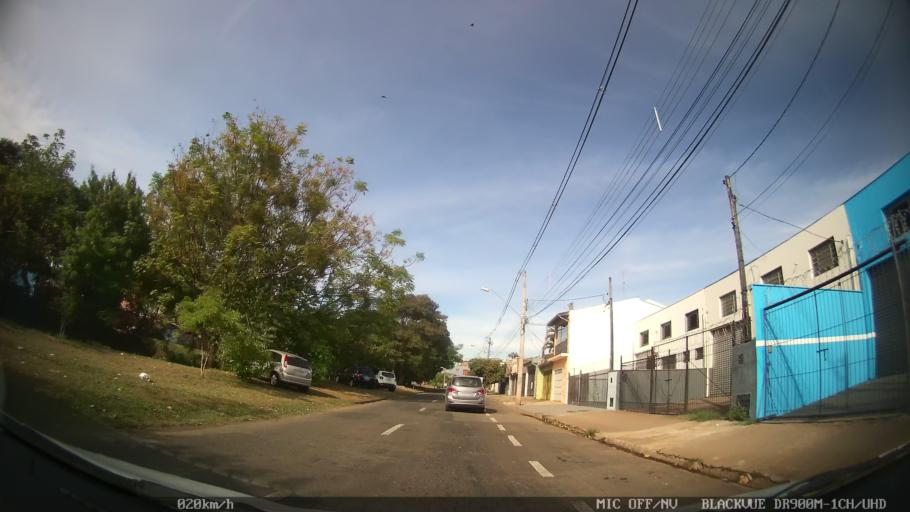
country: BR
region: Sao Paulo
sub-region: Piracicaba
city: Piracicaba
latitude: -22.7385
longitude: -47.6692
